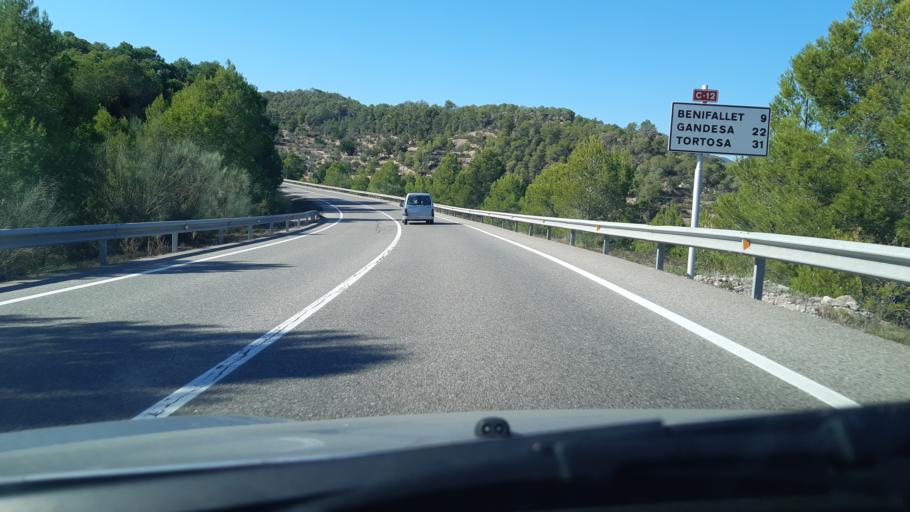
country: ES
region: Catalonia
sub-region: Provincia de Tarragona
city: Rasquera
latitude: 41.0074
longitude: 0.6004
